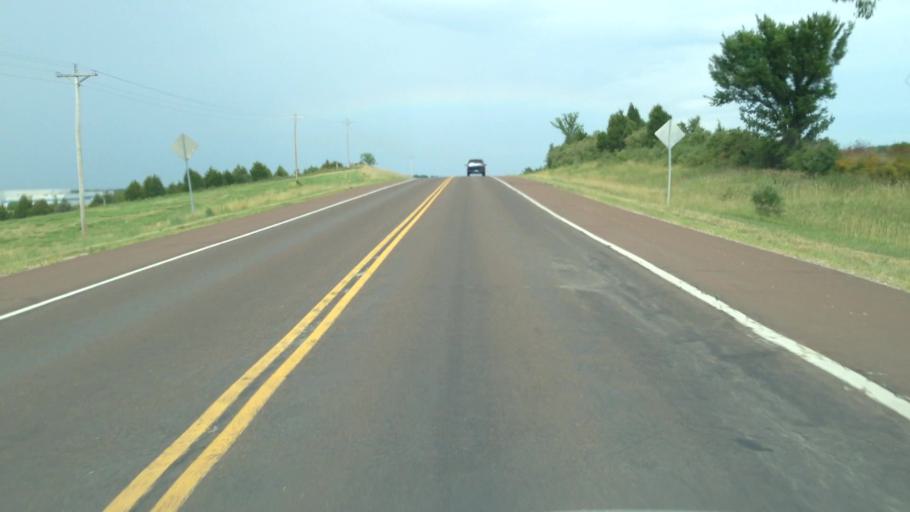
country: US
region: Kansas
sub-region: Douglas County
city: Lawrence
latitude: 39.0006
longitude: -95.3844
